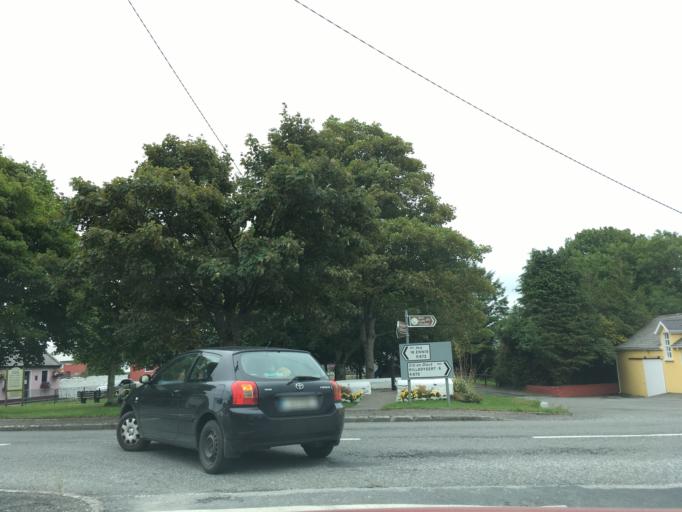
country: IE
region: Munster
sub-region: An Clar
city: Ennis
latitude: 52.7181
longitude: -9.0682
